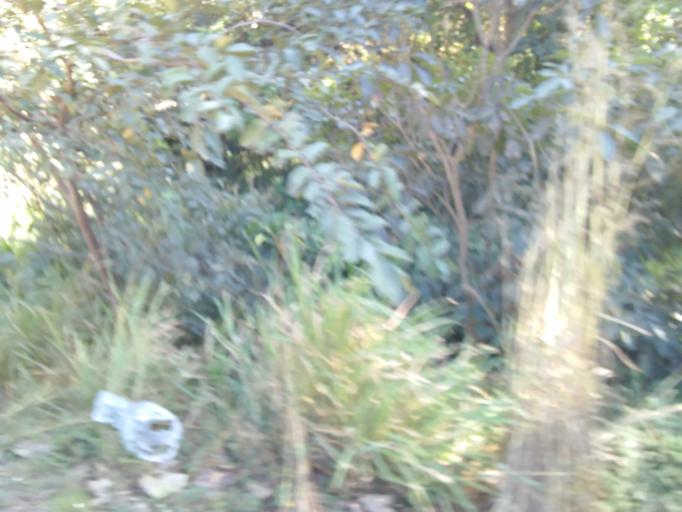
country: MX
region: Nayarit
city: Tepic
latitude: 21.5128
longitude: -104.9162
